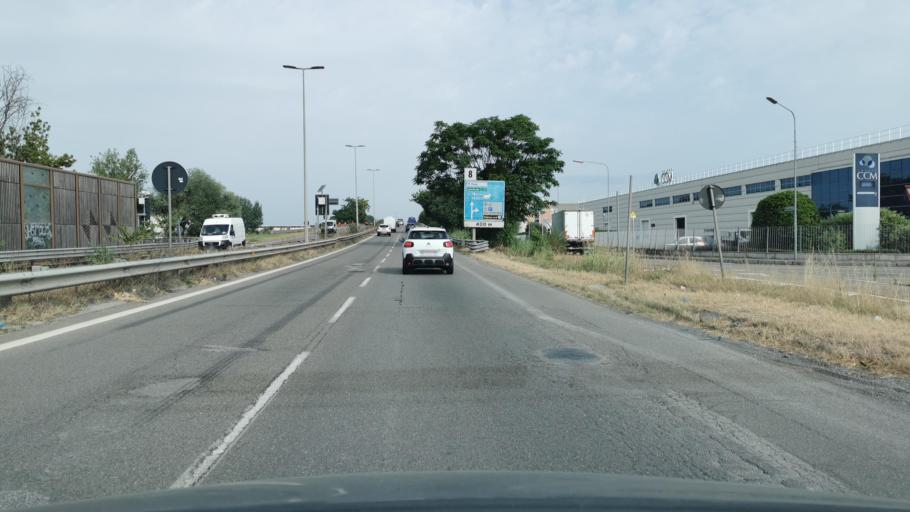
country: IT
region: Emilia-Romagna
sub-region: Provincia di Modena
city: Modena
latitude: 44.6624
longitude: 10.9417
